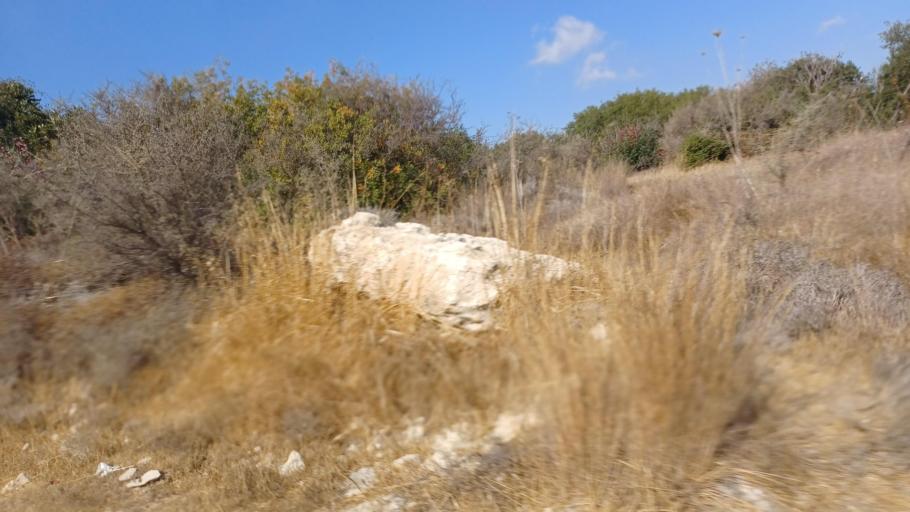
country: CY
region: Pafos
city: Polis
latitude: 34.9767
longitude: 32.4294
